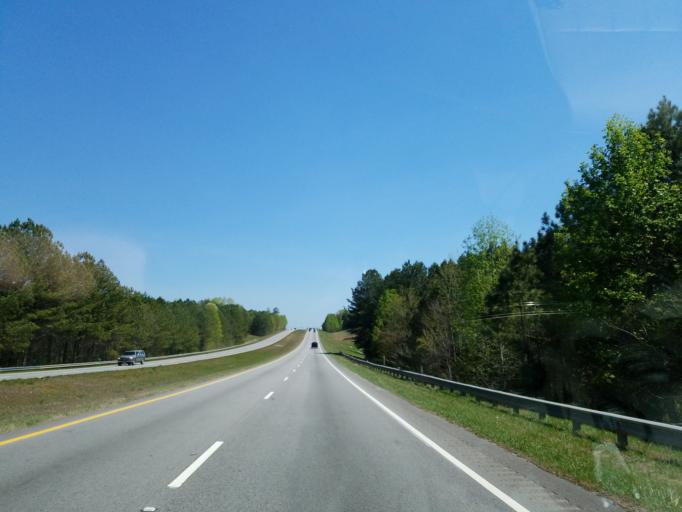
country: US
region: Georgia
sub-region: Paulding County
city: Dallas
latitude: 33.9070
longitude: -84.8186
